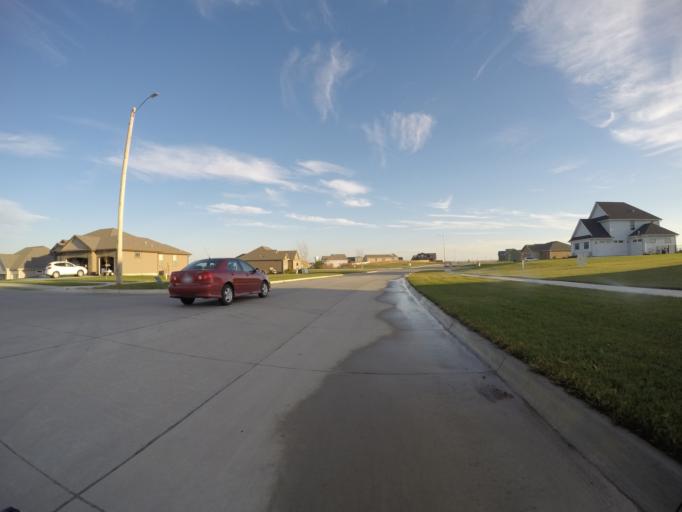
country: US
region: Kansas
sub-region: Riley County
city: Manhattan
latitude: 39.1739
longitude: -96.6353
